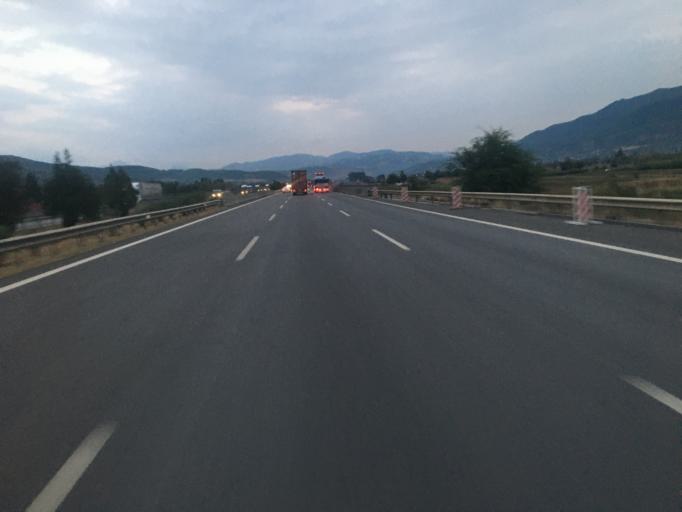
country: TR
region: Osmaniye
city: Osmaniye
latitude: 37.1297
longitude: 36.3027
